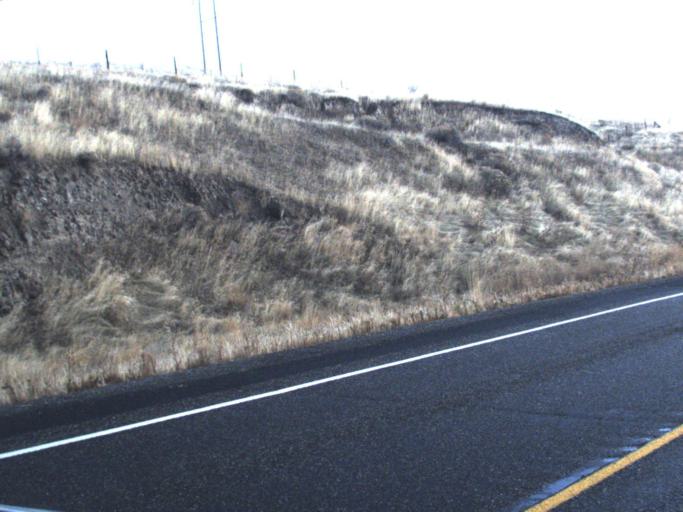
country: US
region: Washington
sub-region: Asotin County
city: Clarkston Heights-Vineland
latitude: 46.4258
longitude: -117.2922
